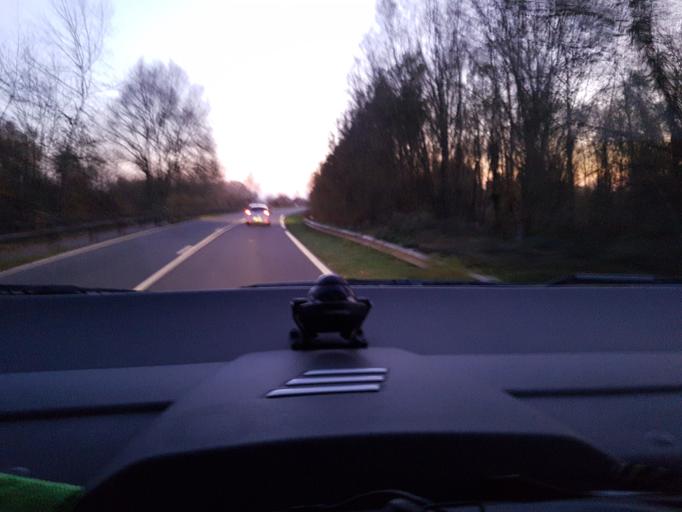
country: FR
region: Picardie
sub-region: Departement de la Somme
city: Saint-Valery-sur-Somme
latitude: 50.1872
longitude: 1.6992
